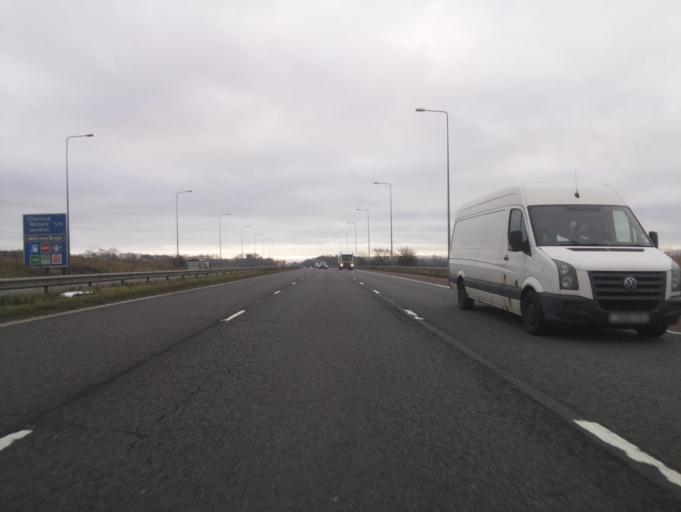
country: GB
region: England
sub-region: Lancashire
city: Euxton
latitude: 53.6418
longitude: -2.6928
